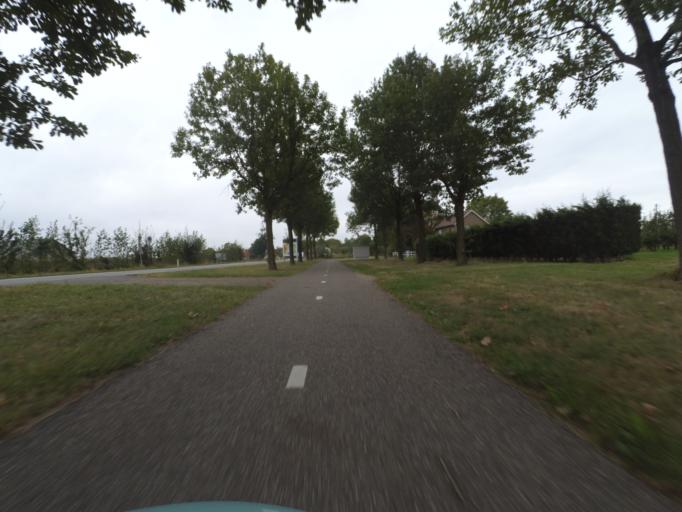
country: NL
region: Gelderland
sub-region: Gemeente Geldermalsen
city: Geldermalsen
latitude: 51.9191
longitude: 5.3290
